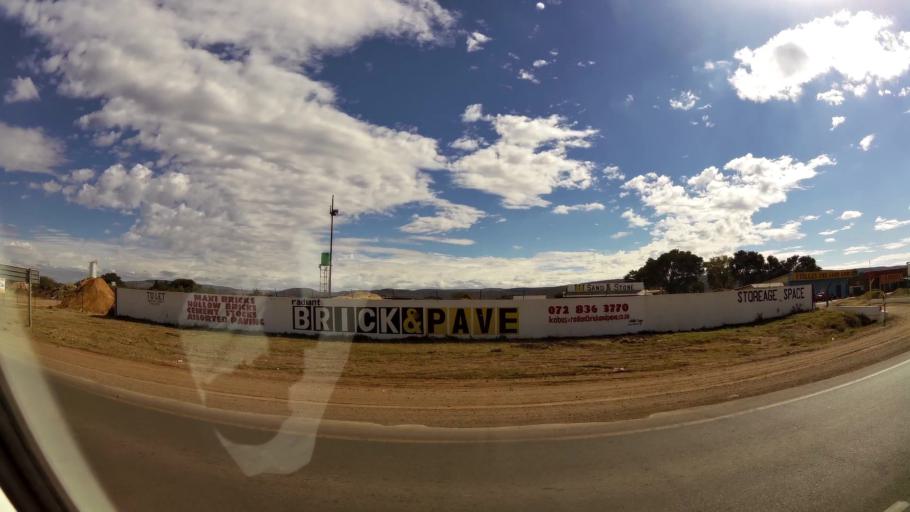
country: ZA
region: Limpopo
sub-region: Waterberg District Municipality
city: Bela-Bela
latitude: -24.8771
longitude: 28.3138
